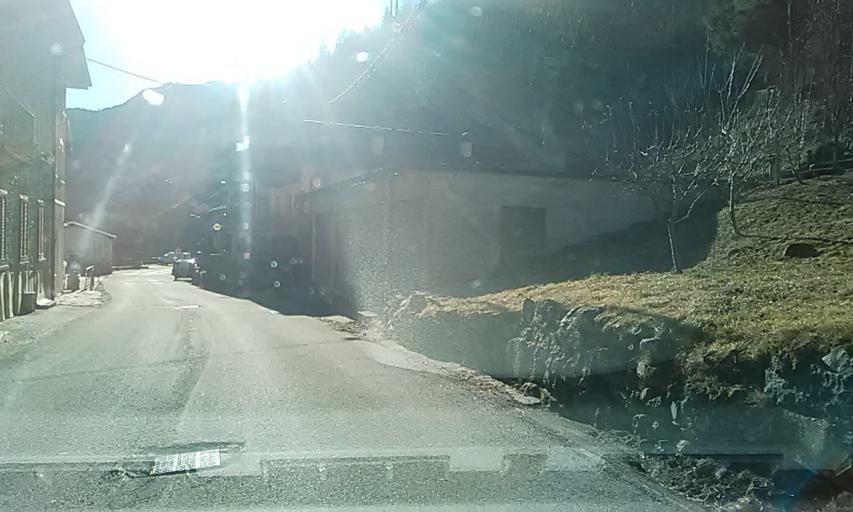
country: IT
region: Piedmont
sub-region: Provincia di Vercelli
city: Rimasco
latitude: 45.8574
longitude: 8.0630
